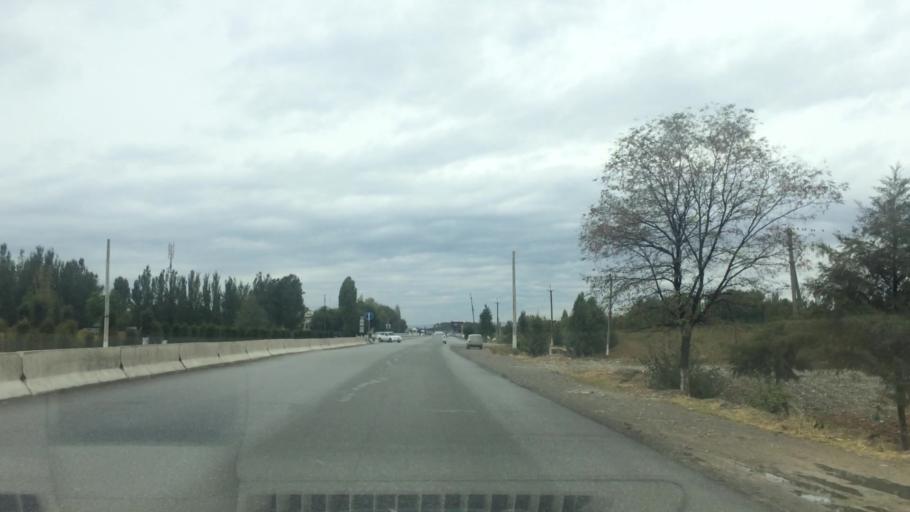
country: UZ
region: Jizzax
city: Jizzax
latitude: 40.0145
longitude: 67.6048
